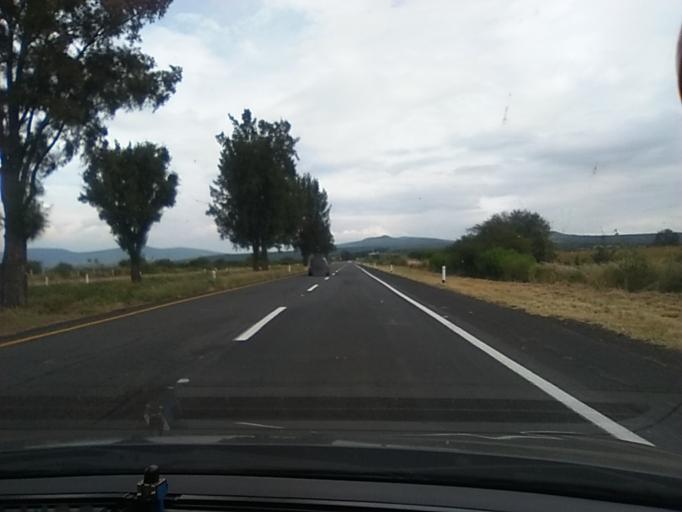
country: MX
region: Michoacan
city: Vistahermosa de Negrete
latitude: 20.2582
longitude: -102.4257
